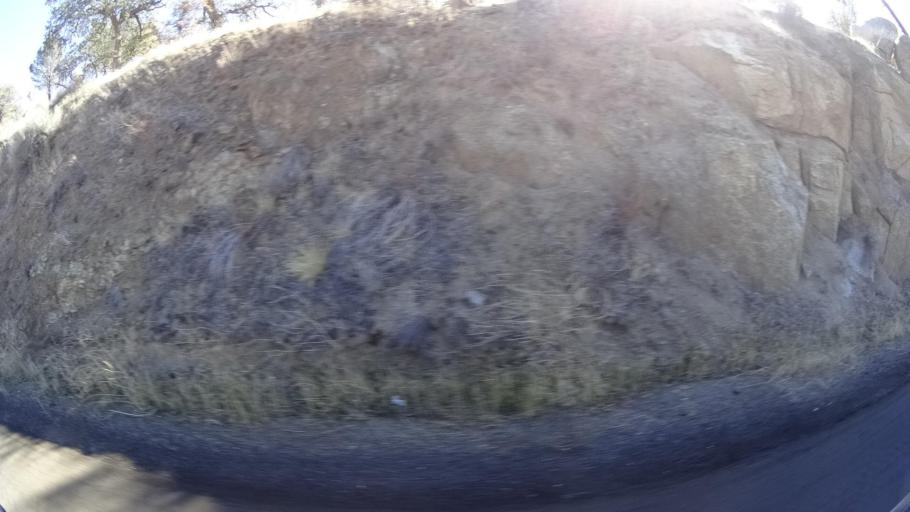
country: US
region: California
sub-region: Kern County
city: Bodfish
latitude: 35.5933
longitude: -118.5131
